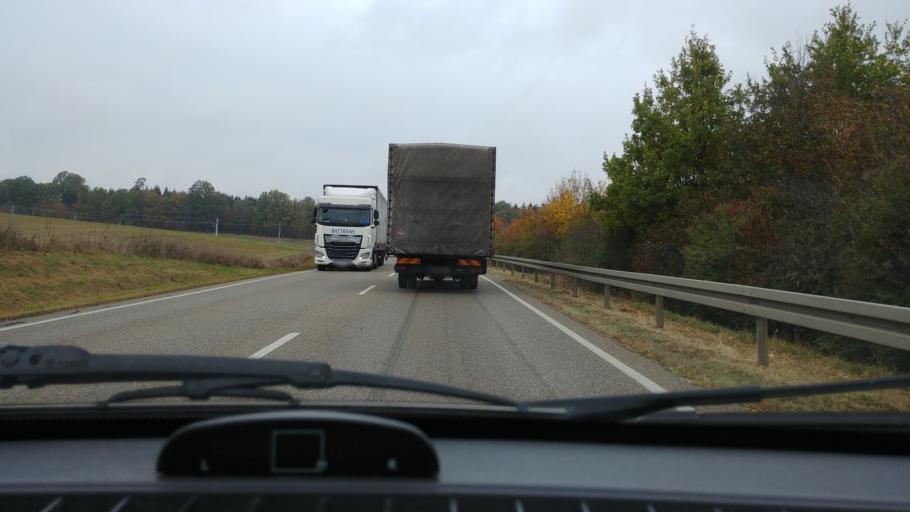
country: DE
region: Baden-Wuerttemberg
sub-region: Regierungsbezirk Stuttgart
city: Aalen
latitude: 48.8486
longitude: 10.0704
